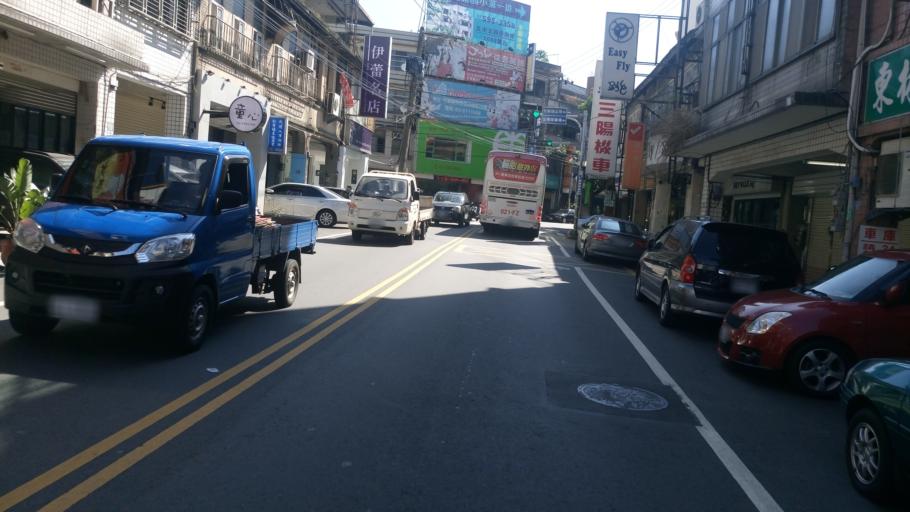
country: TW
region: Taiwan
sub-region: Hsinchu
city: Zhubei
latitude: 24.7370
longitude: 121.0882
